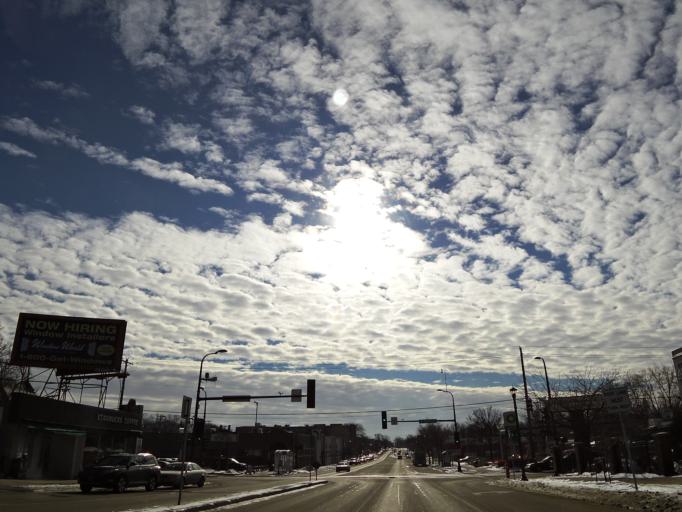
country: US
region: Minnesota
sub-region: Hennepin County
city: Richfield
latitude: 44.9056
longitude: -93.2884
